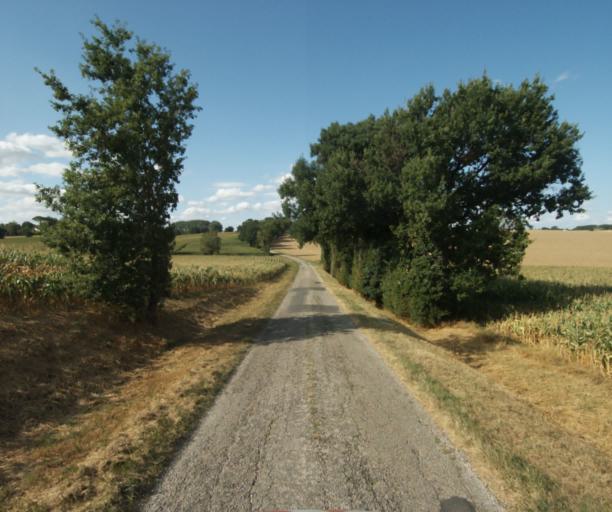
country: FR
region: Midi-Pyrenees
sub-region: Departement du Tarn
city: Puylaurens
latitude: 43.5226
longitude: 1.9888
